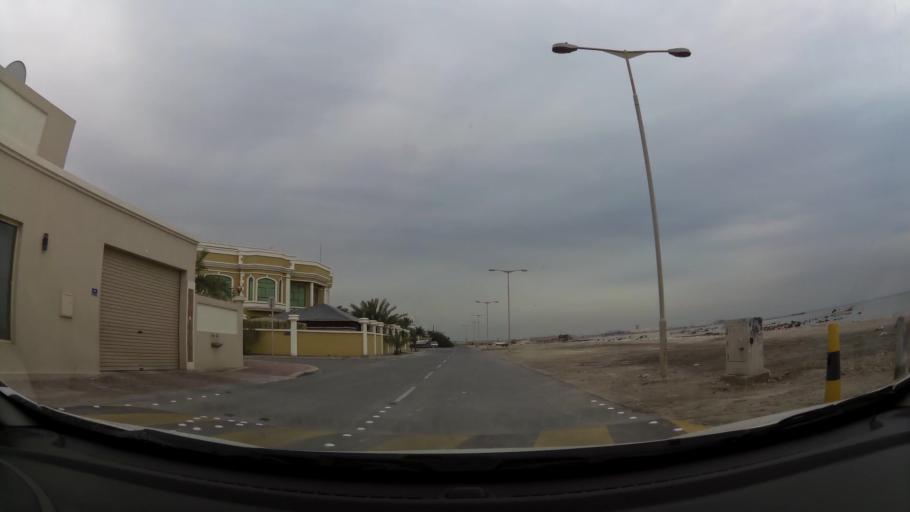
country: BH
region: Northern
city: Ar Rifa'
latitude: 26.0590
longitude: 50.6186
